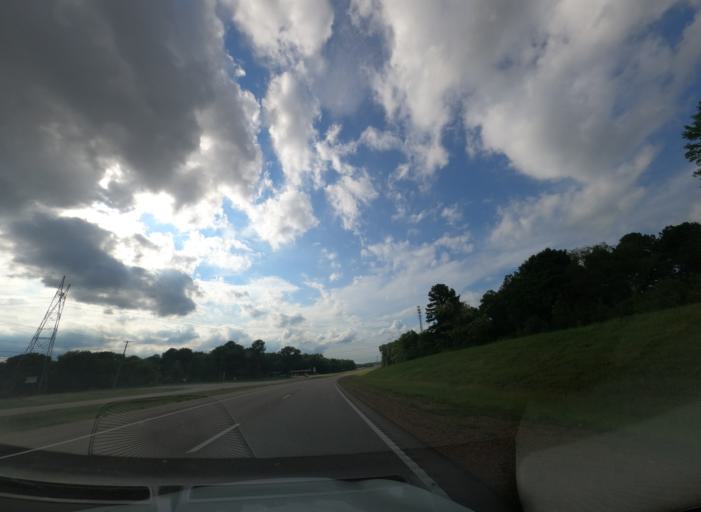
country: US
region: Tennessee
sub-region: Fayette County
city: Piperton
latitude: 34.9900
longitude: -89.6109
